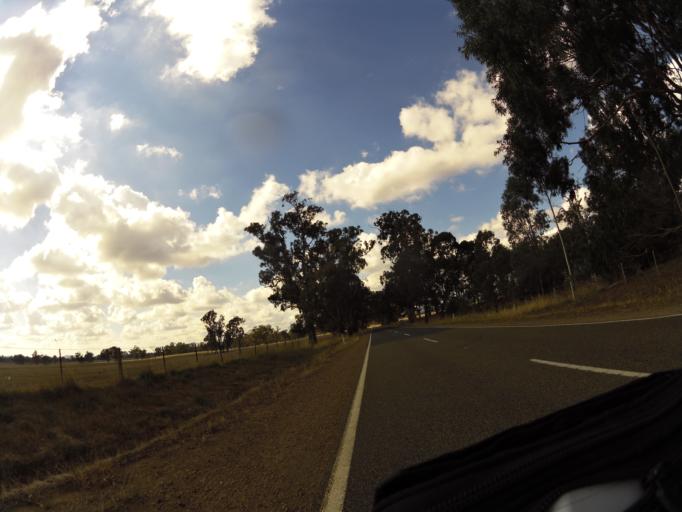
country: AU
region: Victoria
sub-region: Benalla
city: Benalla
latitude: -36.6142
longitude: 146.0254
